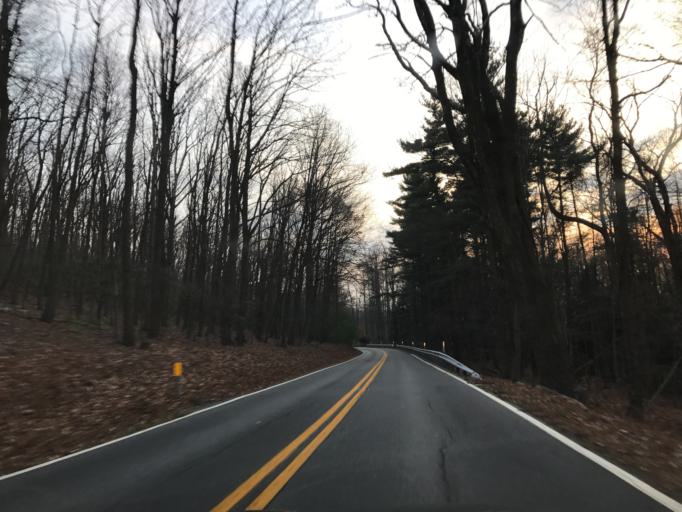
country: US
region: Maryland
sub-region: Frederick County
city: Braddock Heights
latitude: 39.4578
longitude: -77.4909
